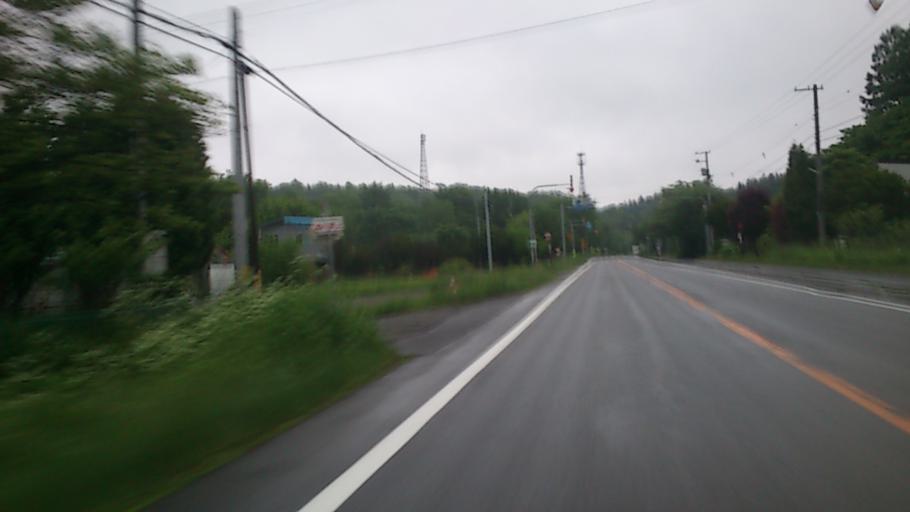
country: JP
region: Hokkaido
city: Chitose
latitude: 42.8116
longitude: 141.5906
